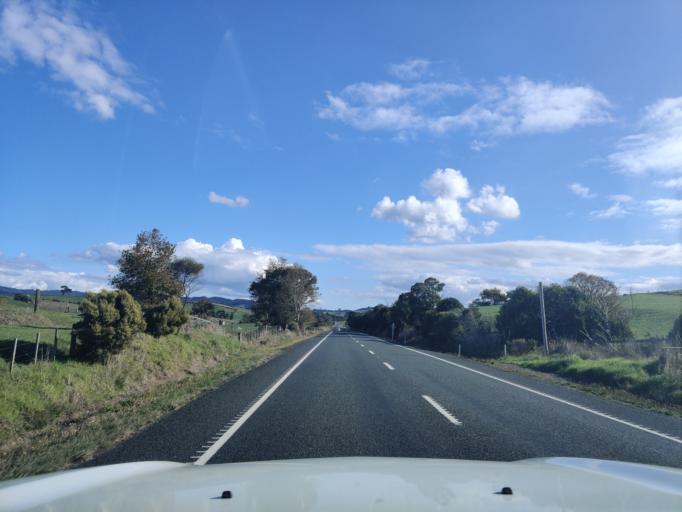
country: NZ
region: Waikato
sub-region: Hauraki District
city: Ngatea
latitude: -37.2833
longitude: 175.3992
